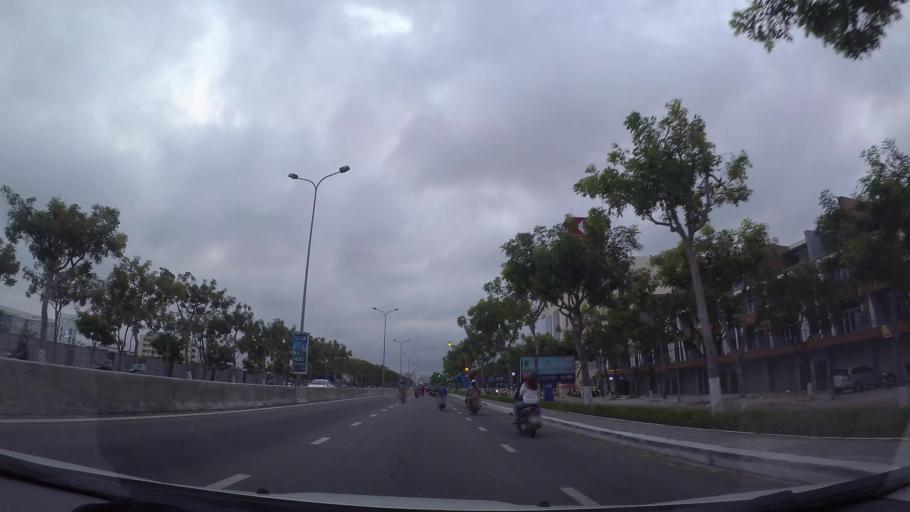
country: VN
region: Da Nang
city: Son Tra
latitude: 16.0348
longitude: 108.2311
